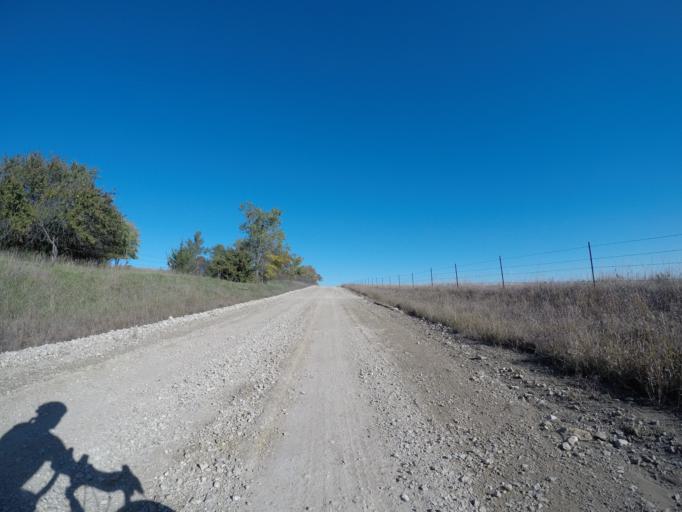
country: US
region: Kansas
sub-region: Wabaunsee County
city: Alma
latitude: 38.8748
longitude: -96.4097
